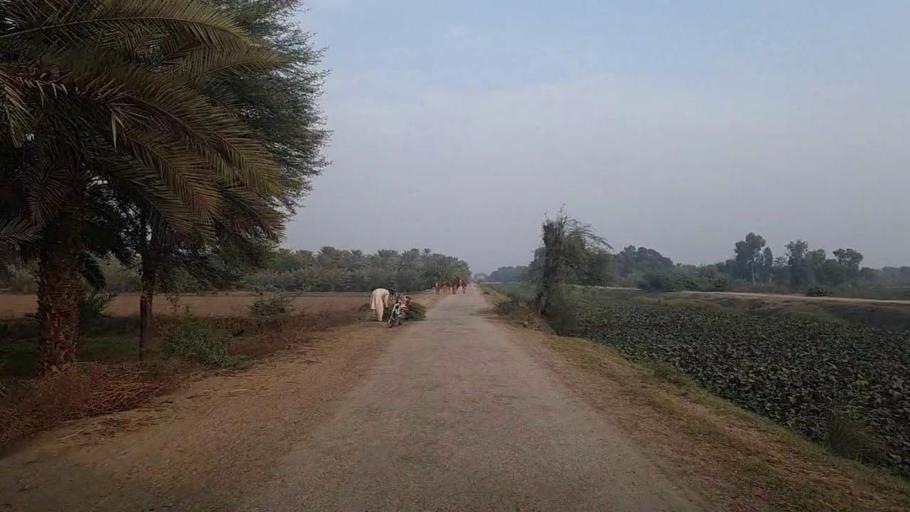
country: PK
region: Sindh
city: Kot Diji
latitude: 27.3584
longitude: 68.6492
